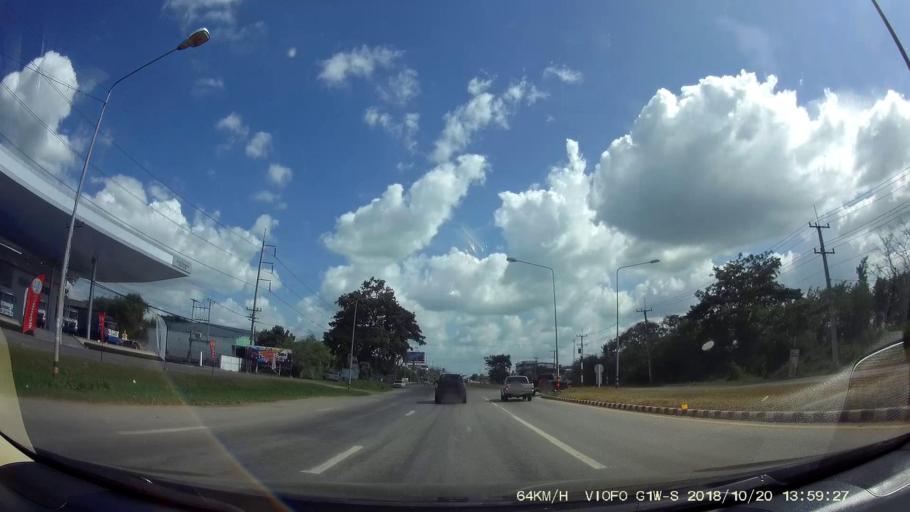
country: TH
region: Khon Kaen
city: Chum Phae
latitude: 16.5243
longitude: 102.1128
